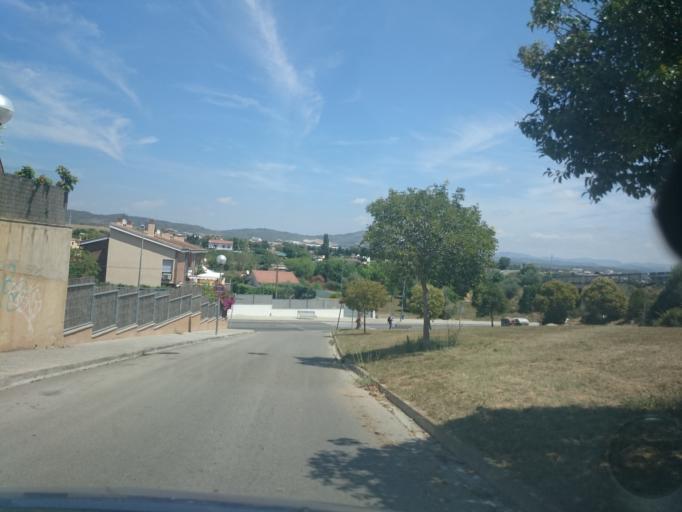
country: ES
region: Catalonia
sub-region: Provincia de Barcelona
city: Vilanova i la Geltru
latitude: 41.2244
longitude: 1.7009
